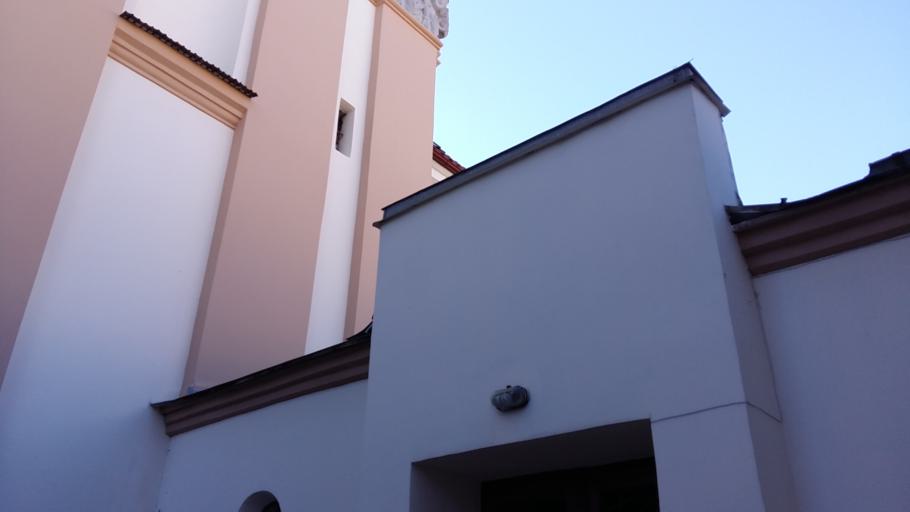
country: BY
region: Grodnenskaya
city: Hrodna
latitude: 53.6772
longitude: 23.8360
